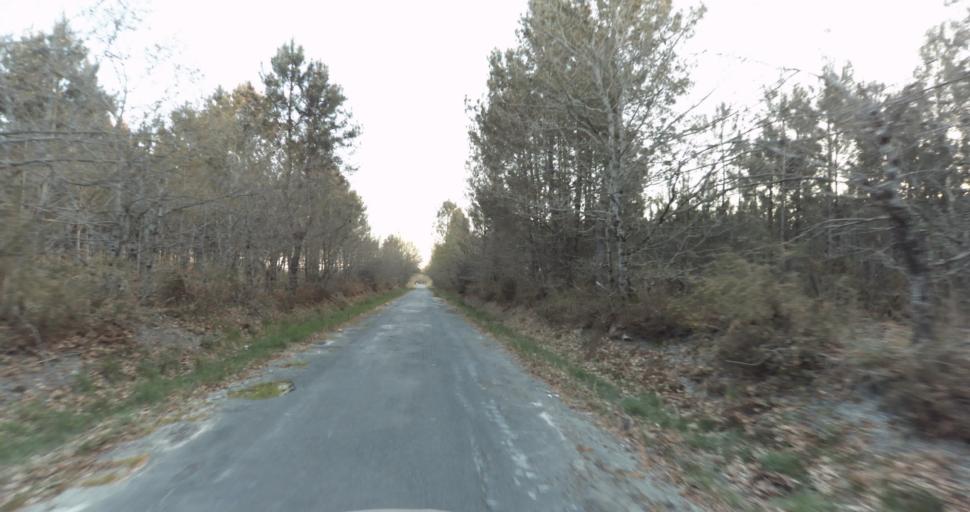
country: FR
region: Aquitaine
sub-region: Departement de la Gironde
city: Martignas-sur-Jalle
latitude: 44.8253
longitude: -0.7409
